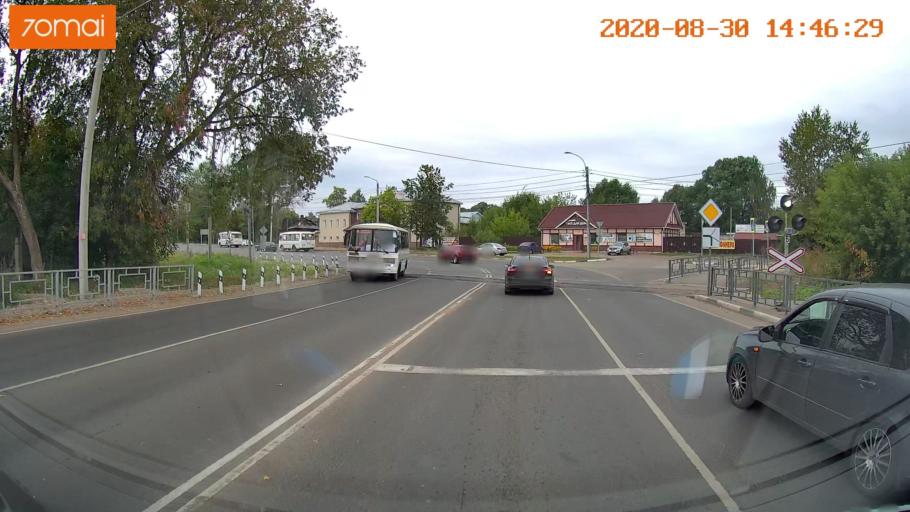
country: RU
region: Ivanovo
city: Kineshma
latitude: 57.4418
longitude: 42.1424
